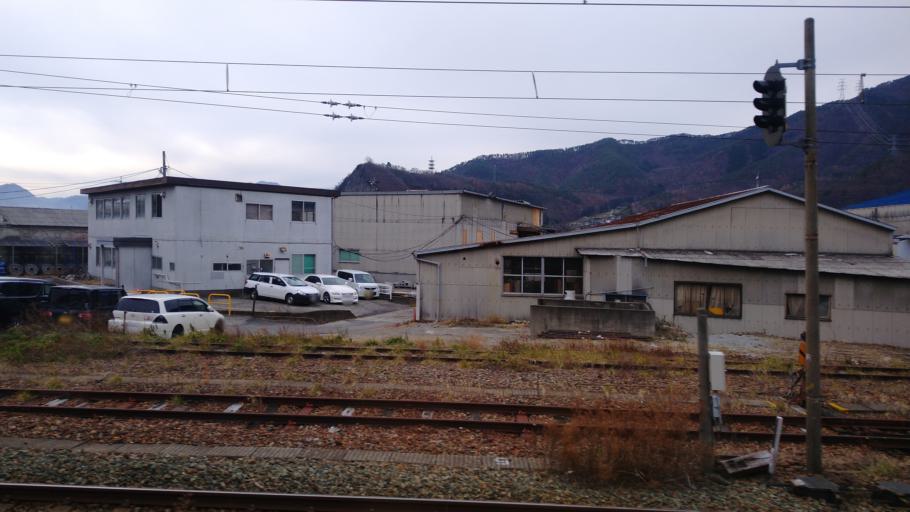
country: JP
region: Nagano
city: Ueda
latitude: 36.4180
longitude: 138.2063
